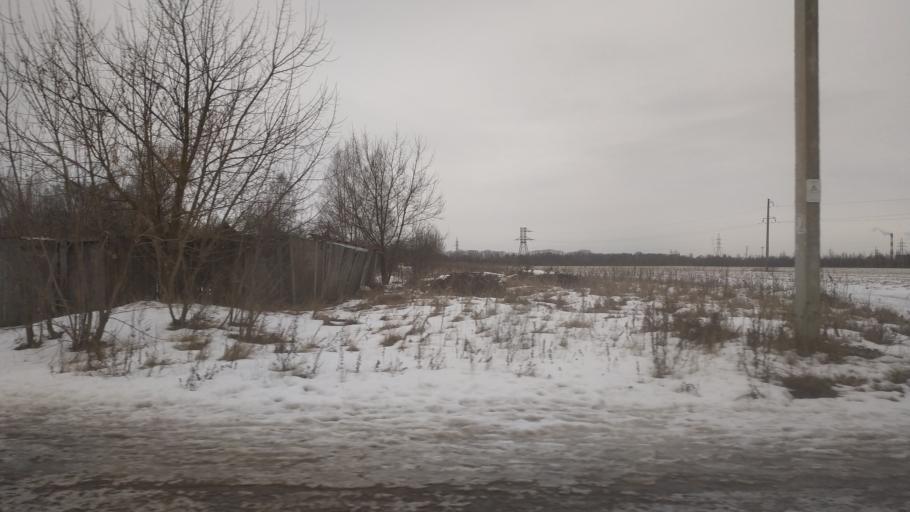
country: RU
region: Tverskaya
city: Tver
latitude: 56.8947
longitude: 35.8482
